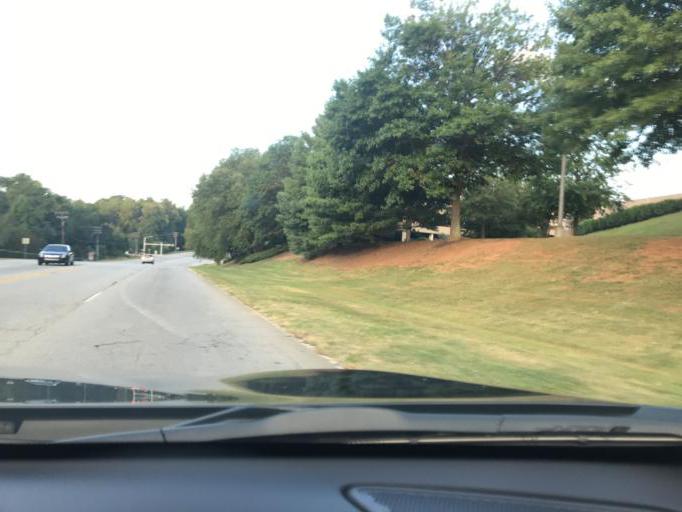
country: US
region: South Carolina
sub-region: Greenville County
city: Dunean
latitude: 34.8175
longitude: -82.4079
